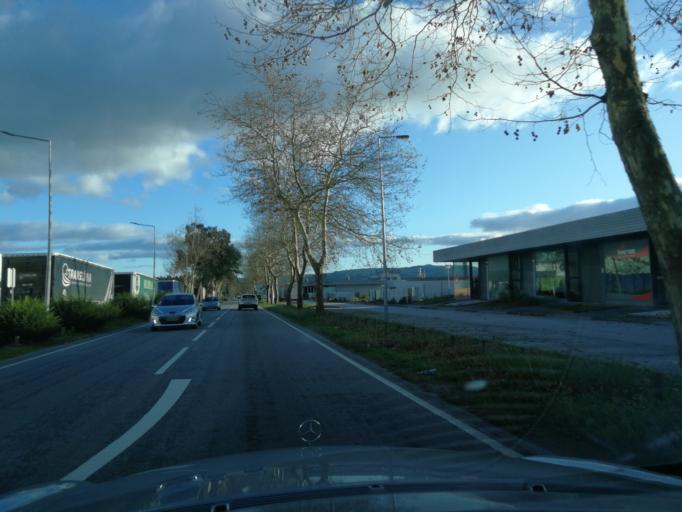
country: PT
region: Viana do Castelo
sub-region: Viana do Castelo
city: Darque
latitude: 41.6364
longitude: -8.7658
